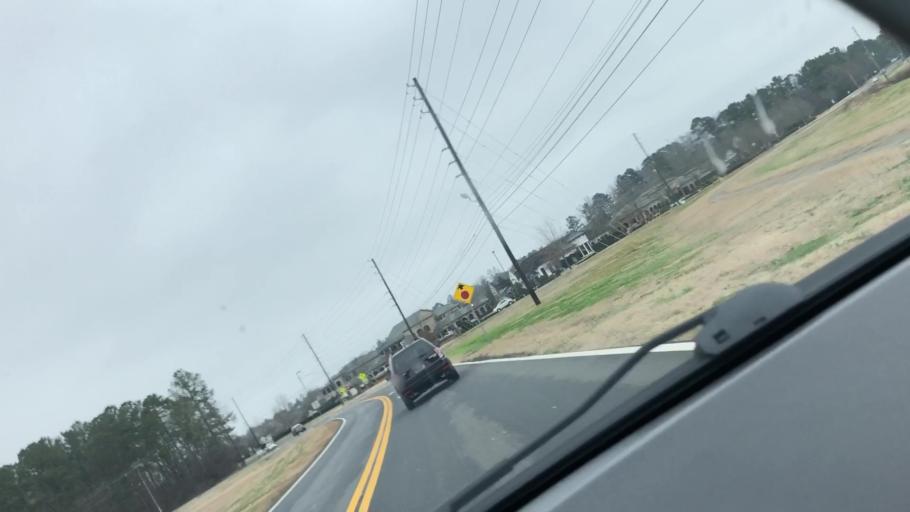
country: US
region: Georgia
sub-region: Bartow County
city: Cartersville
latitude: 34.1353
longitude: -84.8203
